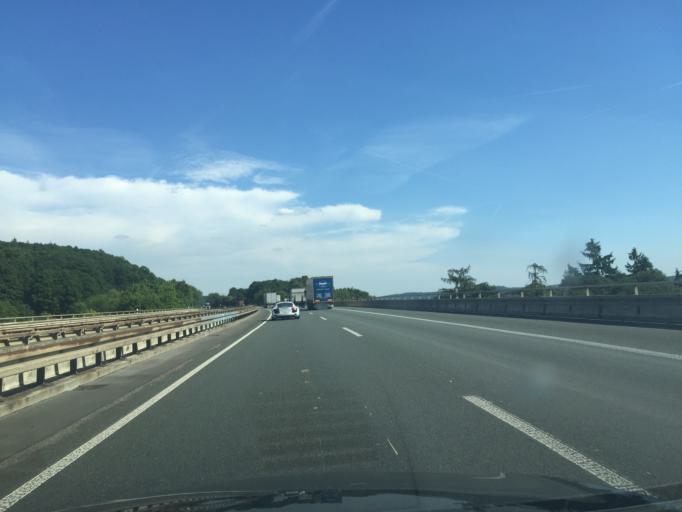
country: DE
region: Hesse
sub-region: Regierungsbezirk Giessen
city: Sinn
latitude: 50.6282
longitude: 8.3361
